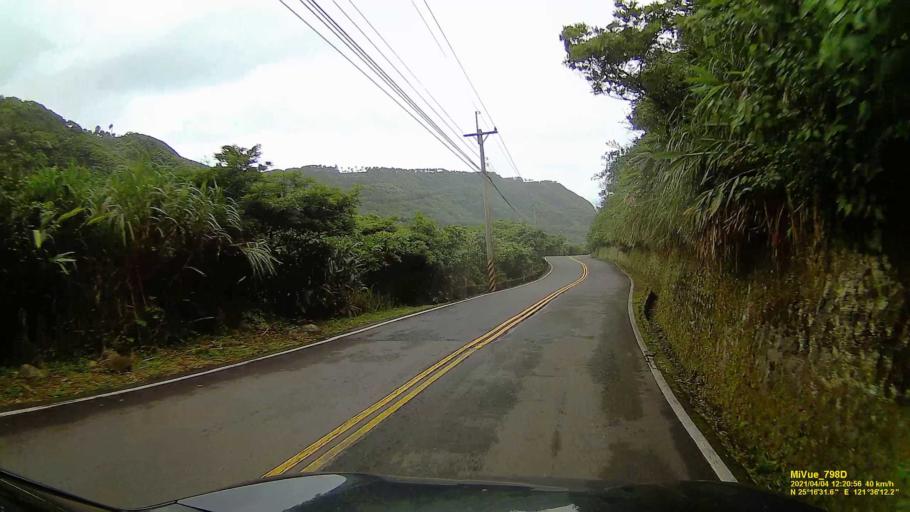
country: TW
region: Taiwan
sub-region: Keelung
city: Keelung
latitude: 25.2758
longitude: 121.6034
